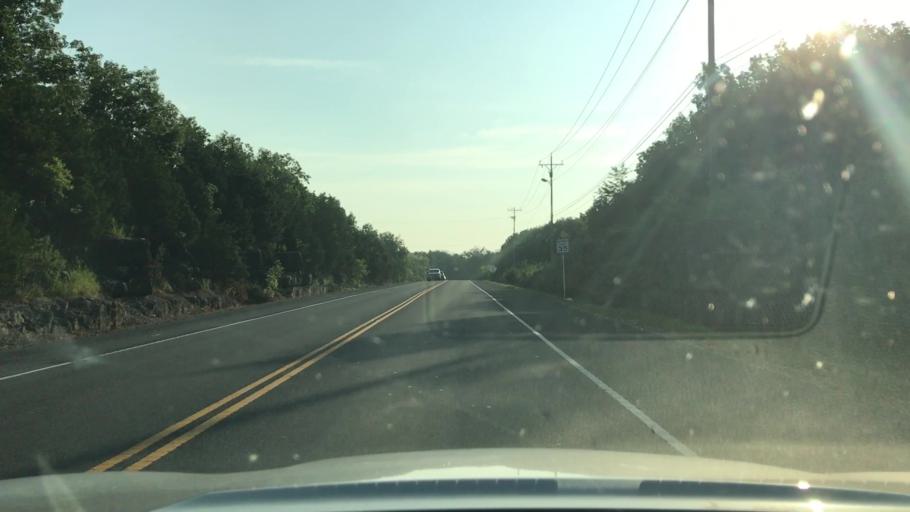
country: US
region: Tennessee
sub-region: Rutherford County
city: La Vergne
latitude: 36.0440
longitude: -86.6045
